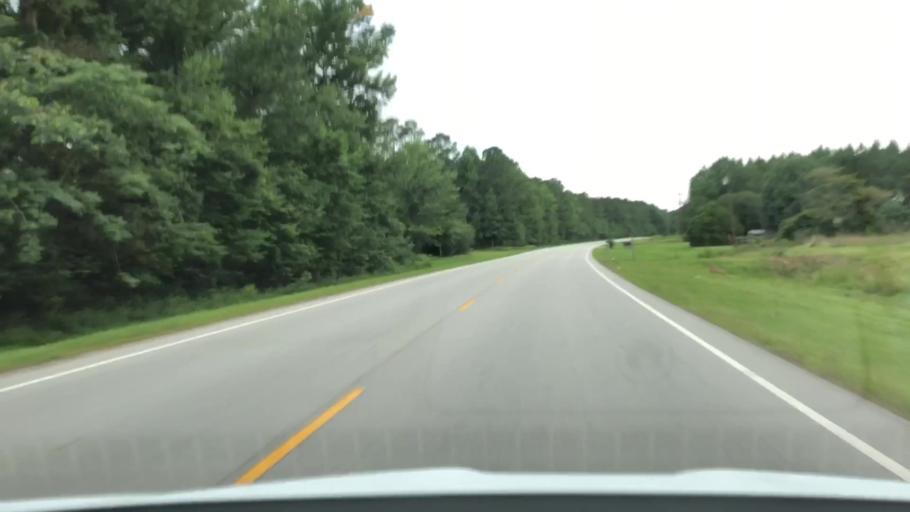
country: US
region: North Carolina
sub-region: Jones County
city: Trenton
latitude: 35.0366
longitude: -77.3429
